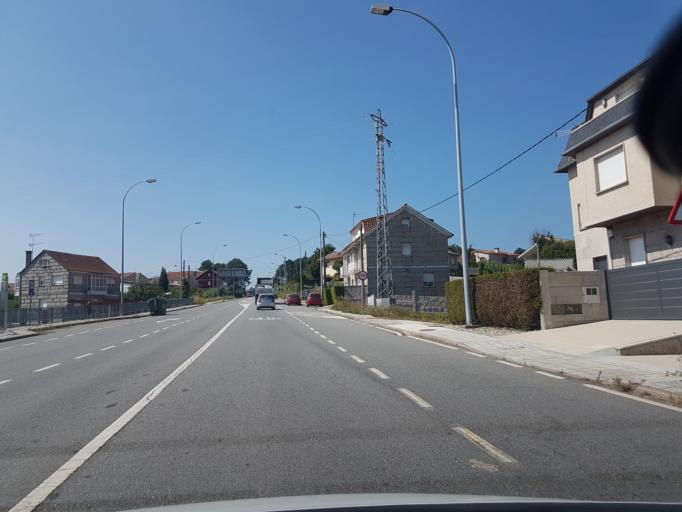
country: ES
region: Galicia
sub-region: Provincia de Pontevedra
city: Redondela
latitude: 42.2304
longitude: -8.6377
